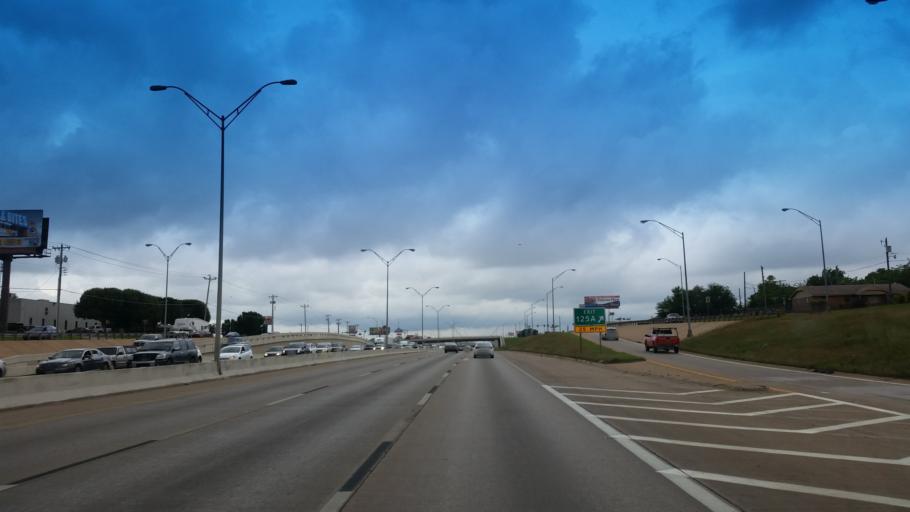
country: US
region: Oklahoma
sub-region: Oklahoma County
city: Oklahoma City
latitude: 35.4428
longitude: -97.4863
